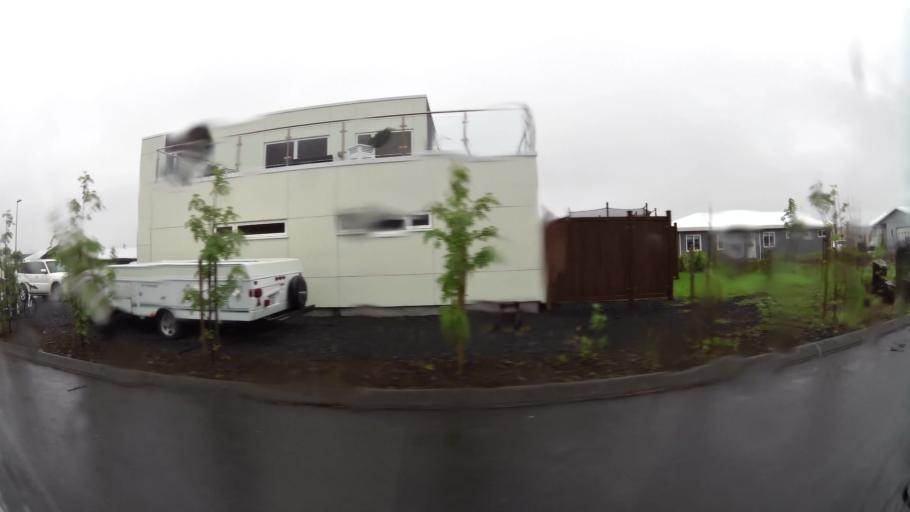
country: IS
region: South
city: Selfoss
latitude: 63.9260
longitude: -21.0109
